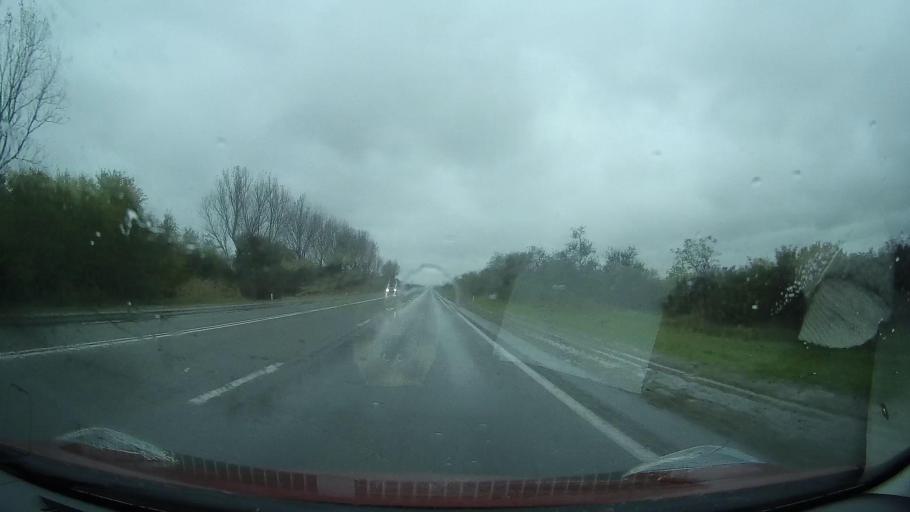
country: RU
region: Stavropol'skiy
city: Nevinnomyssk
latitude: 44.6305
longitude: 42.0290
